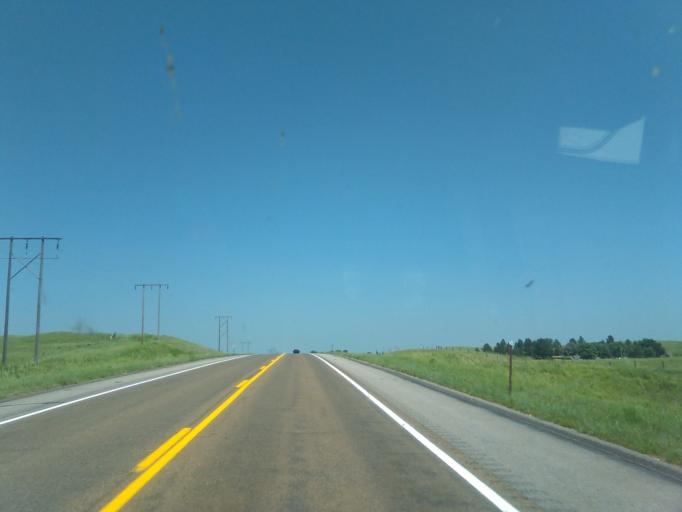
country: US
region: Nebraska
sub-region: Lincoln County
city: North Platte
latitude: 40.8909
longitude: -100.7540
